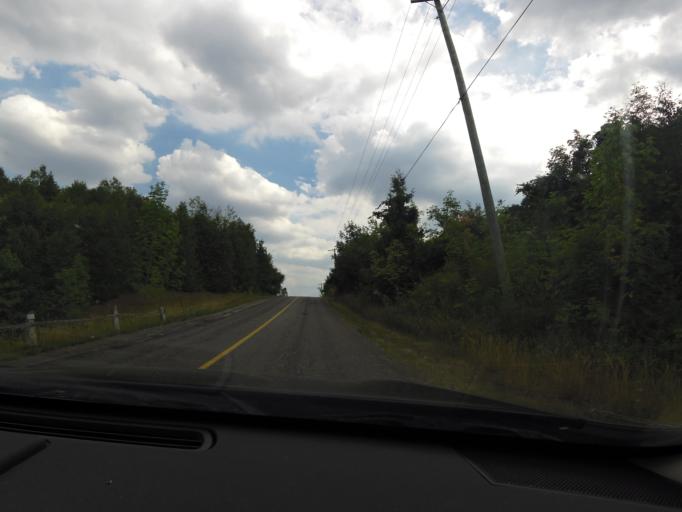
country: CA
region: Ontario
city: Brampton
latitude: 43.7631
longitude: -79.9364
